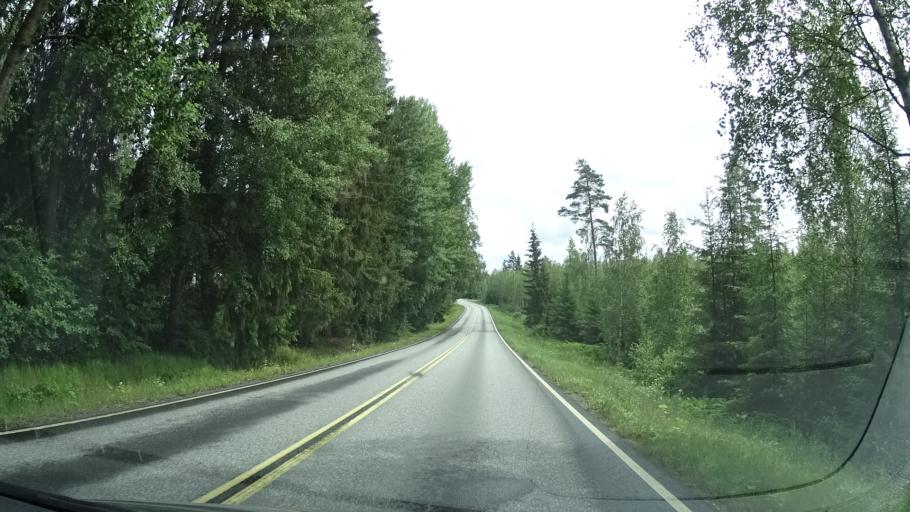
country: FI
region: Pirkanmaa
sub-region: Etelae-Pirkanmaa
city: Urjala
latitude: 61.0859
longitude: 23.4008
